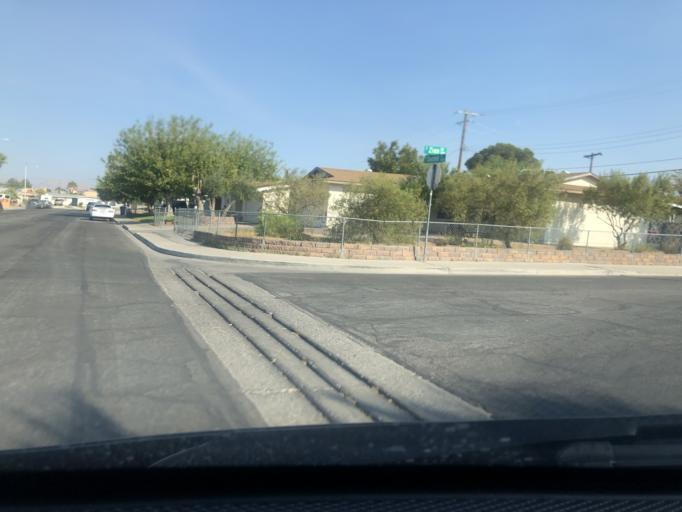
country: US
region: Nevada
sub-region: Clark County
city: Spring Valley
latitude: 36.1727
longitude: -115.2196
